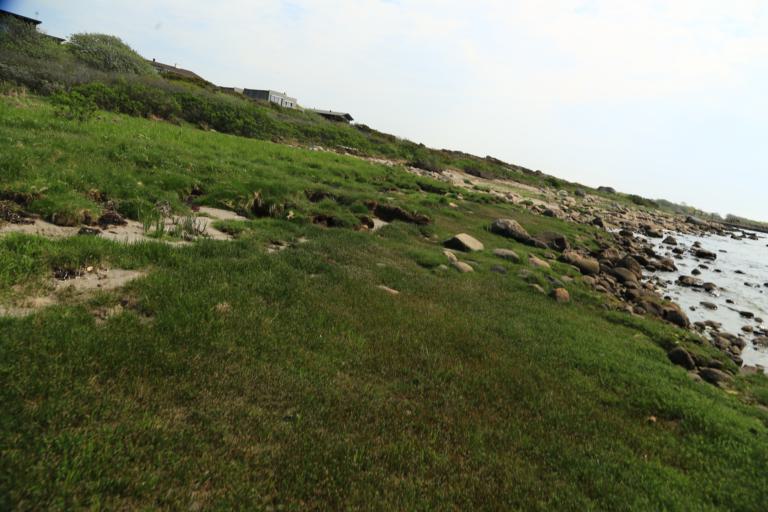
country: SE
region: Halland
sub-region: Varbergs Kommun
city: Varberg
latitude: 57.1427
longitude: 12.2144
